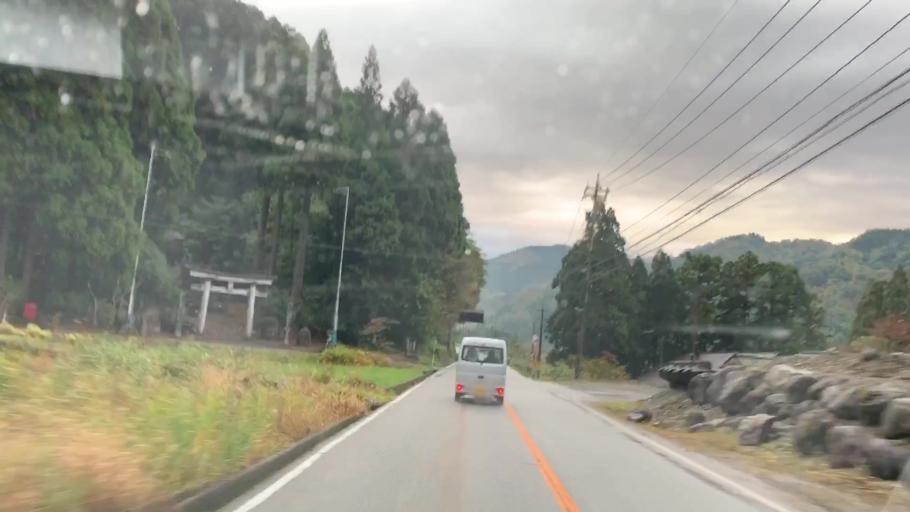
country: JP
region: Toyama
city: Kamiichi
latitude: 36.5819
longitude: 137.3367
